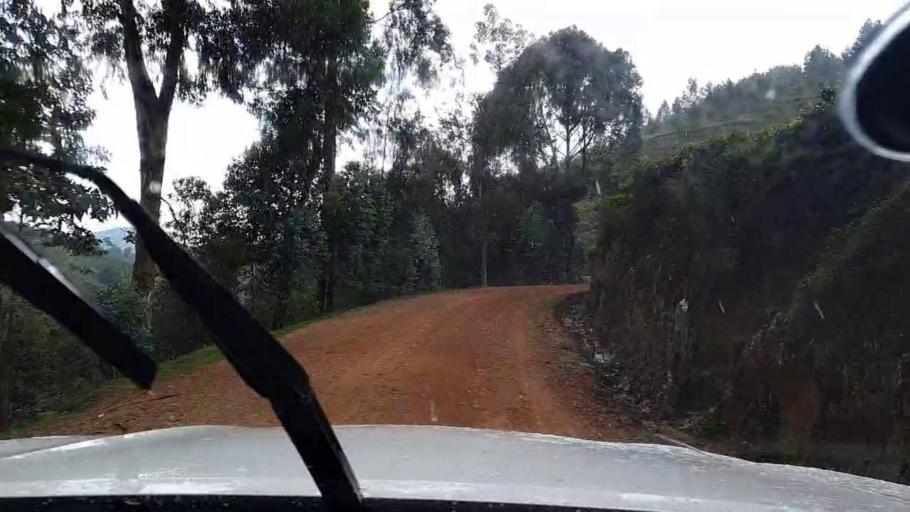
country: RW
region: Western Province
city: Kibuye
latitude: -2.1500
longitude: 29.4275
